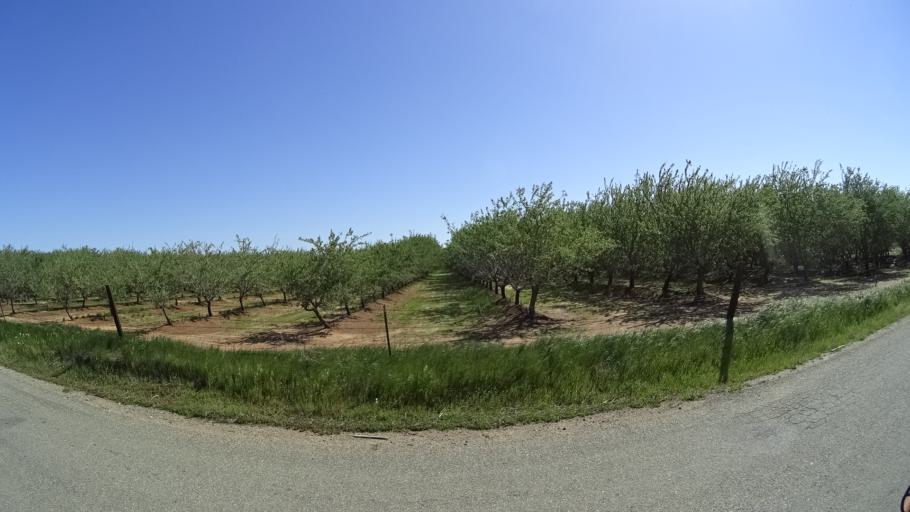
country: US
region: California
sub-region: Glenn County
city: Orland
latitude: 39.6809
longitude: -122.2717
